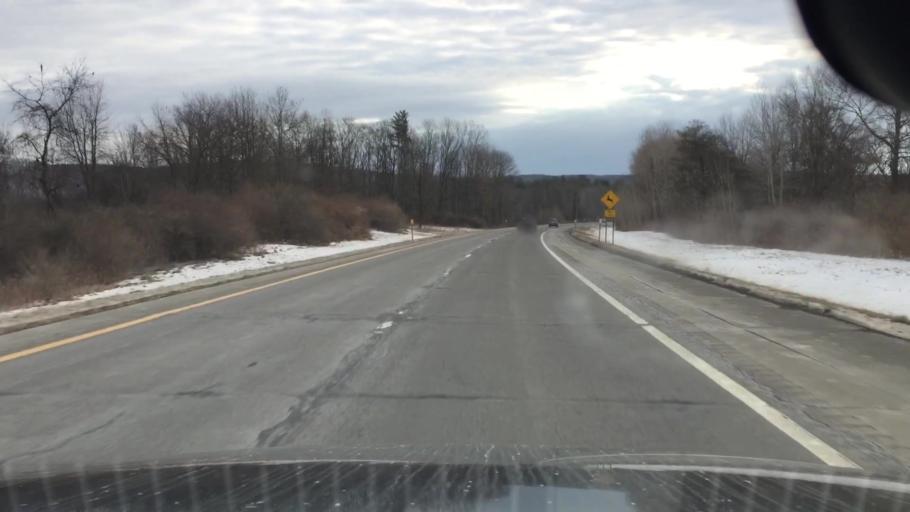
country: US
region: New York
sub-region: Tioga County
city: Apalachin
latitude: 42.0885
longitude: -76.1790
